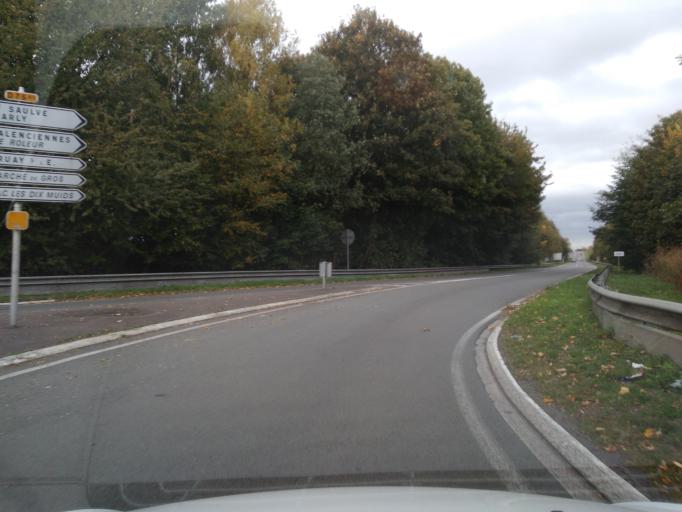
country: FR
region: Nord-Pas-de-Calais
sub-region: Departement du Nord
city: Saultain
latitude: 50.3490
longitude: 3.5729
